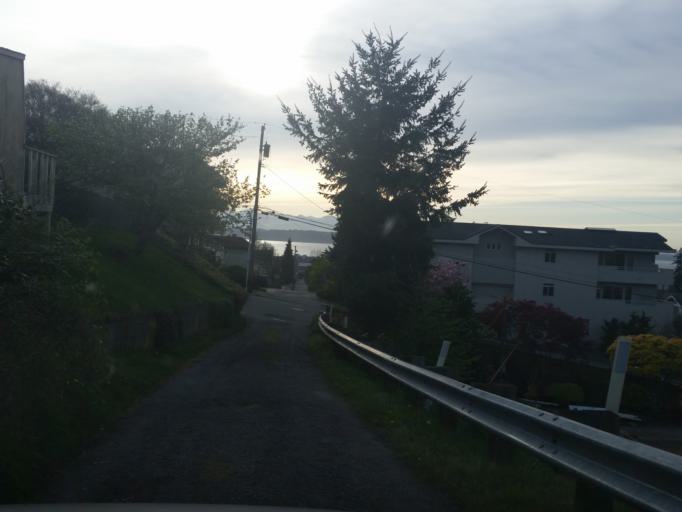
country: US
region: Washington
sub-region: Snohomish County
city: Edmonds
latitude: 47.8109
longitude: -122.3716
